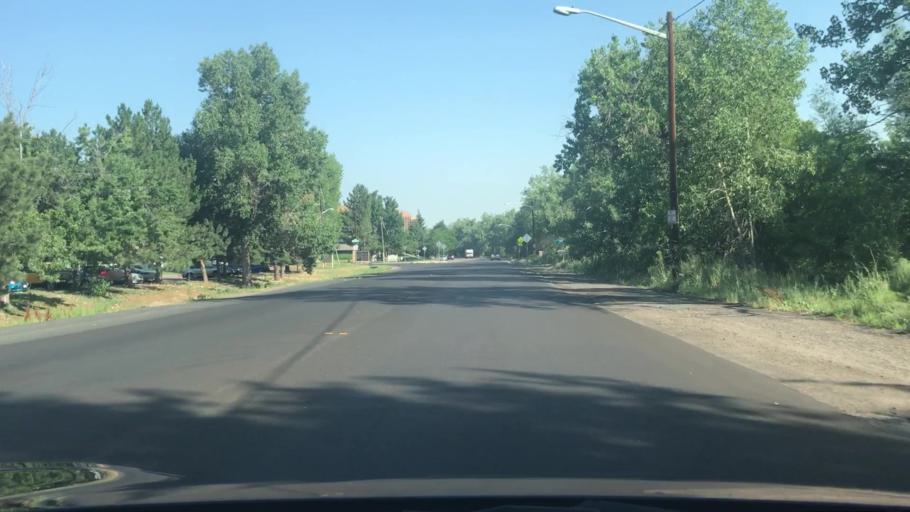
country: US
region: Colorado
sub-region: Arapahoe County
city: Glendale
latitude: 39.6994
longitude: -104.9265
